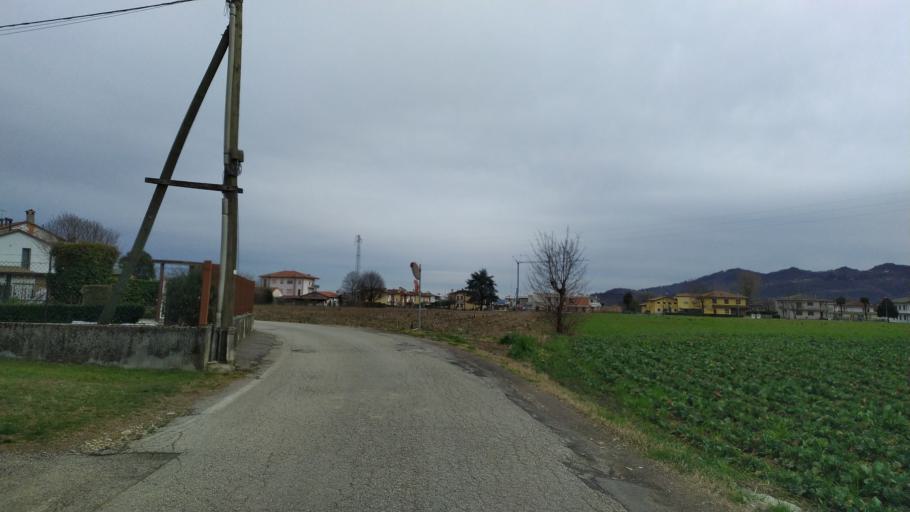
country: IT
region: Veneto
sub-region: Provincia di Vicenza
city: Malo
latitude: 45.6567
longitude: 11.4200
